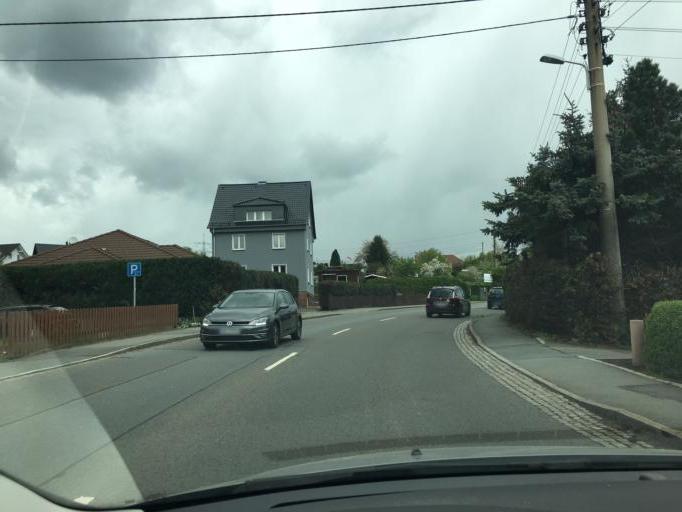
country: DE
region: Saxony
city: Hohenstein-Ernstthal
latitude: 50.8096
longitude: 12.7569
